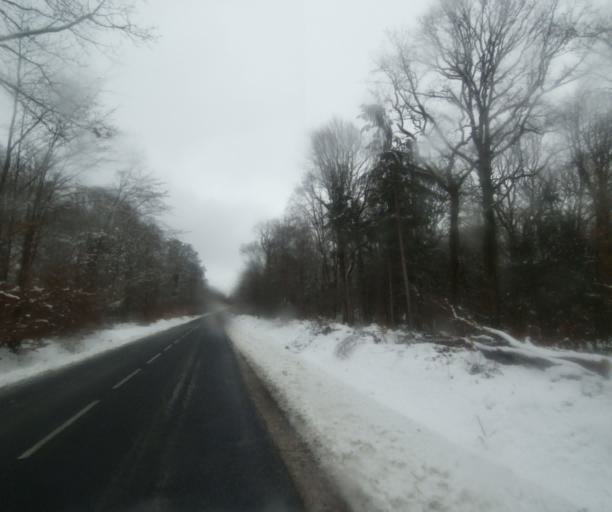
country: FR
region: Champagne-Ardenne
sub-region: Departement de la Haute-Marne
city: Laneuville-a-Remy
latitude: 48.4581
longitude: 4.8845
